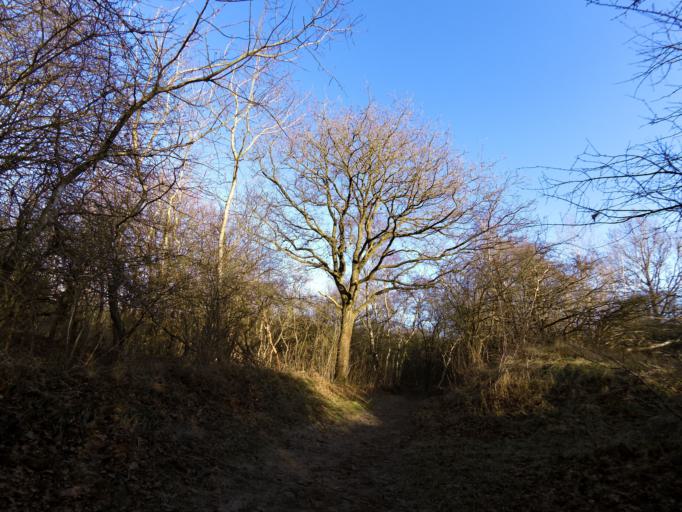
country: NL
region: South Holland
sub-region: Gemeente Hellevoetsluis
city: Nieuw-Helvoet
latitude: 51.9033
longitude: 4.0619
